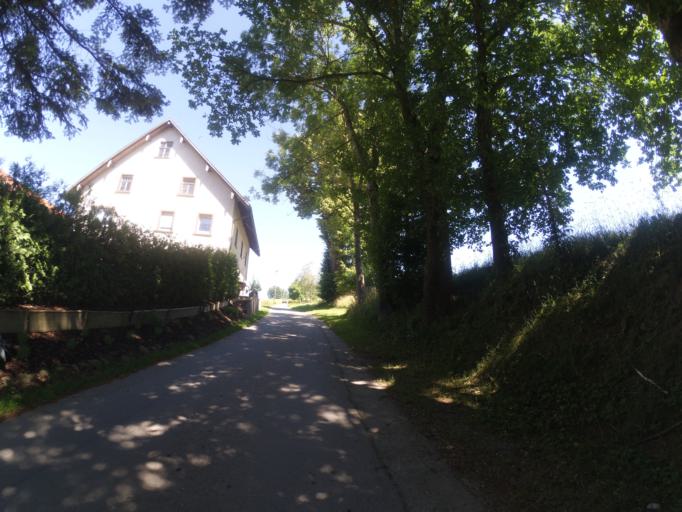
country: DE
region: Baden-Wuerttemberg
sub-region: Tuebingen Region
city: Bad Wurzach
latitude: 47.8925
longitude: 9.9060
